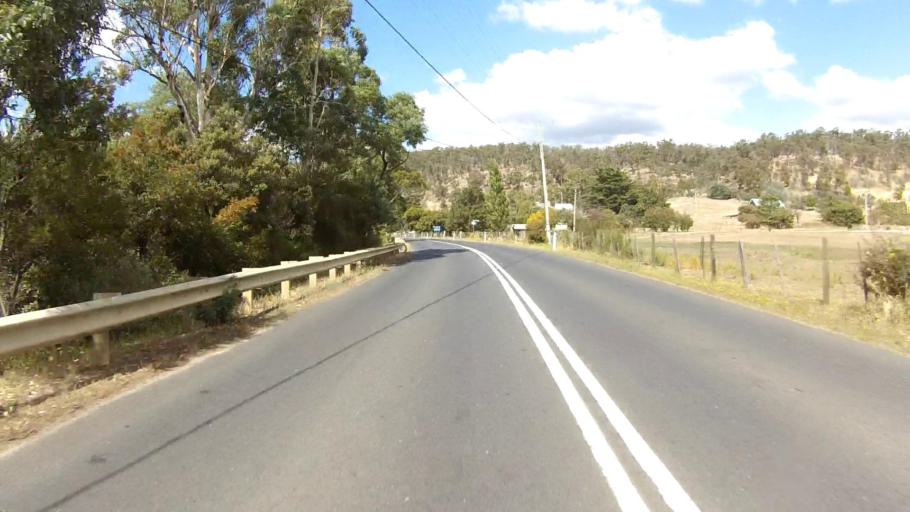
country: AU
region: Tasmania
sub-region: Derwent Valley
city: New Norfolk
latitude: -42.7746
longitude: 147.0277
